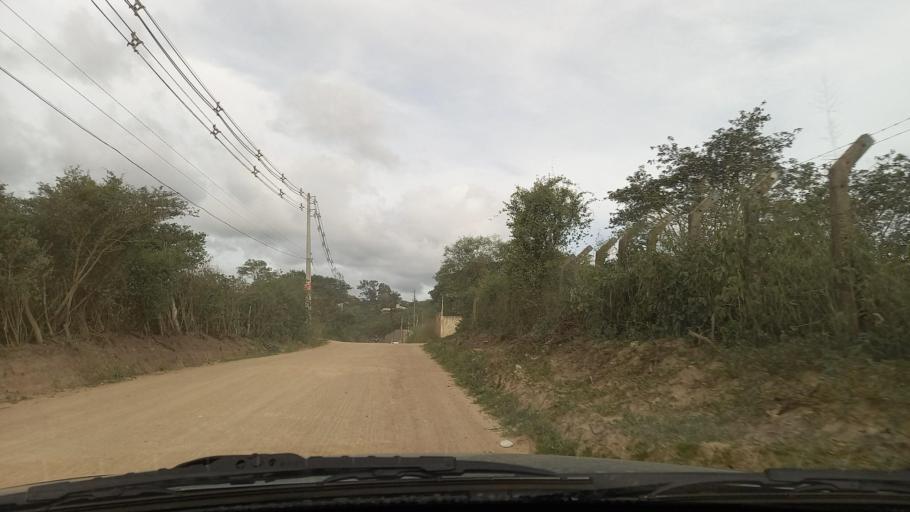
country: BR
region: Pernambuco
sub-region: Gravata
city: Gravata
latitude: -8.1981
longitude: -35.5361
